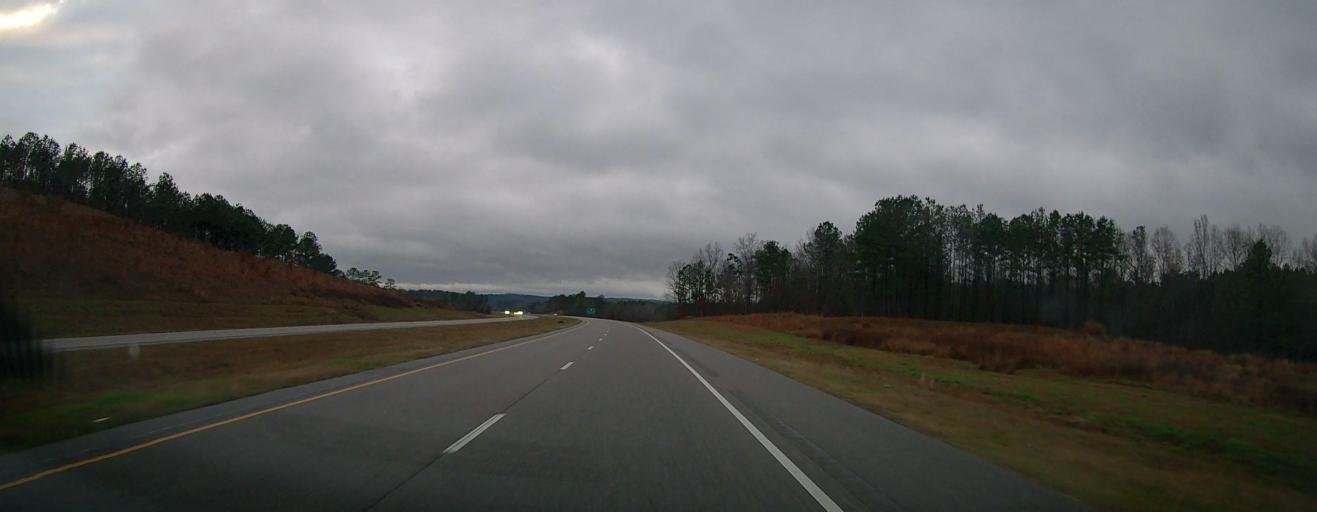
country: US
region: Alabama
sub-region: Bibb County
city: Centreville
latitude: 32.9538
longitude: -87.1134
